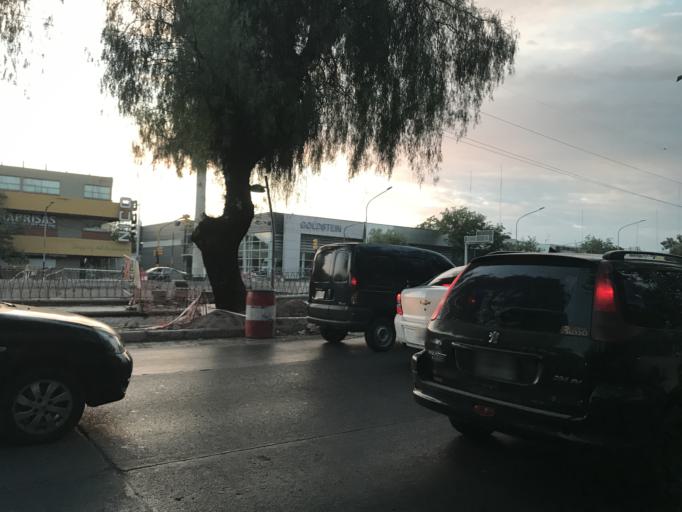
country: AR
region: Mendoza
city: Mendoza
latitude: -32.8899
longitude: -68.8302
